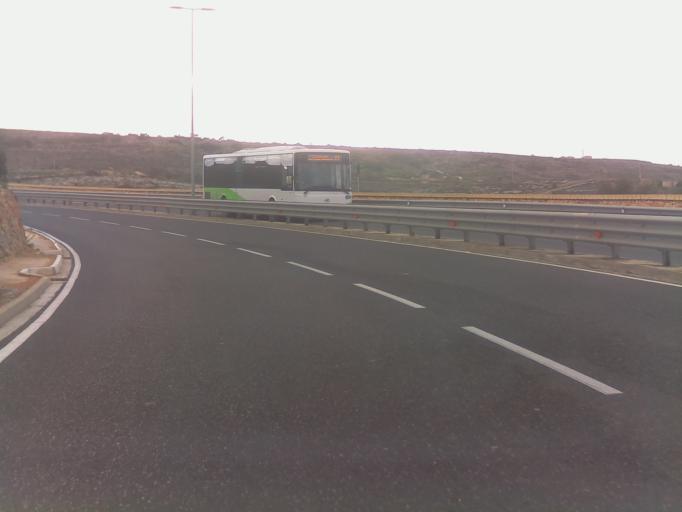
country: MT
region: Il-Mellieha
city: Mellieha
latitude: 35.9820
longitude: 14.3412
